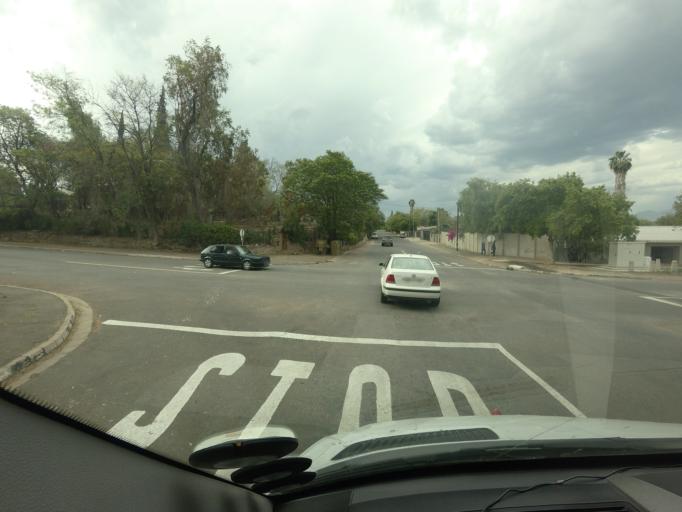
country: ZA
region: Western Cape
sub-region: Eden District Municipality
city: Oudtshoorn
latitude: -33.5832
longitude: 22.1959
